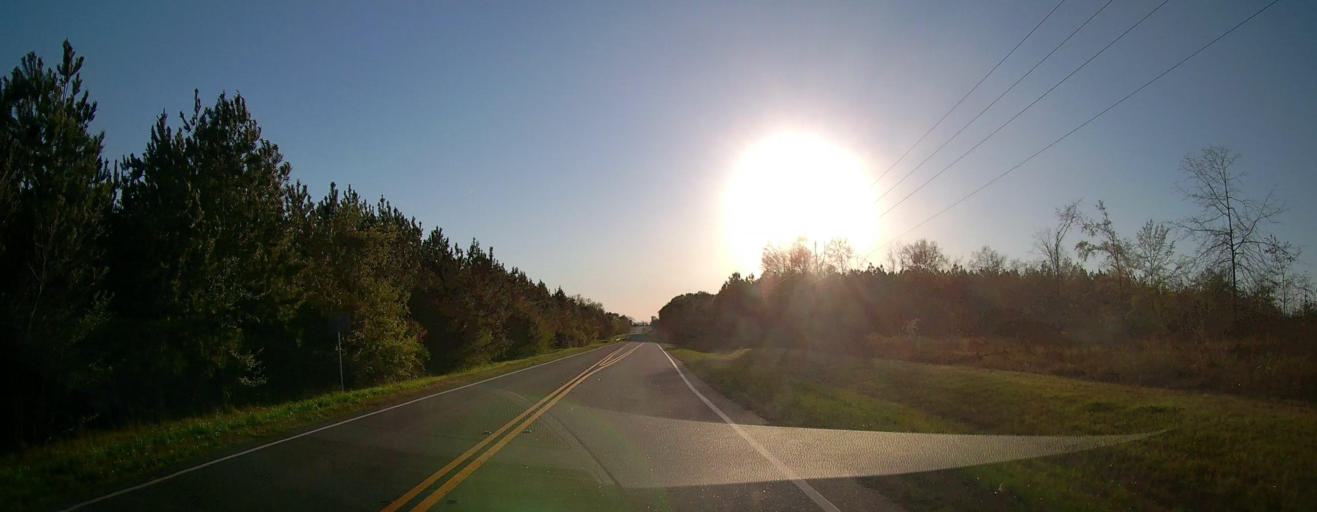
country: US
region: Georgia
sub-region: Wilcox County
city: Rochelle
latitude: 31.9659
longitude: -83.3870
